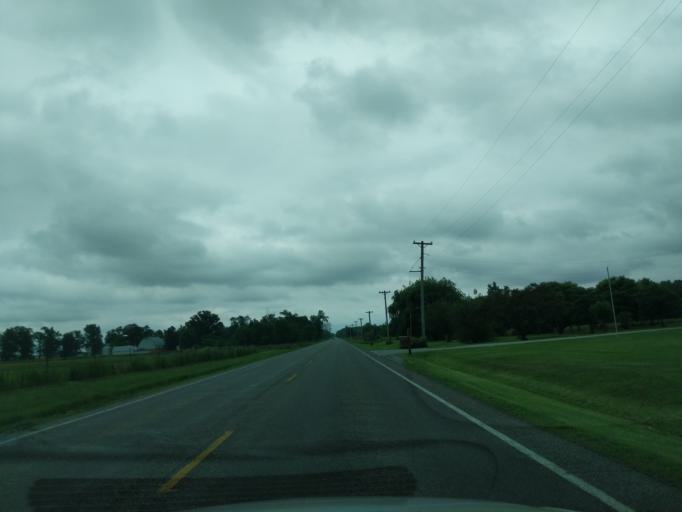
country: US
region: Indiana
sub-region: Tipton County
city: Tipton
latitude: 40.2833
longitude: -85.9846
